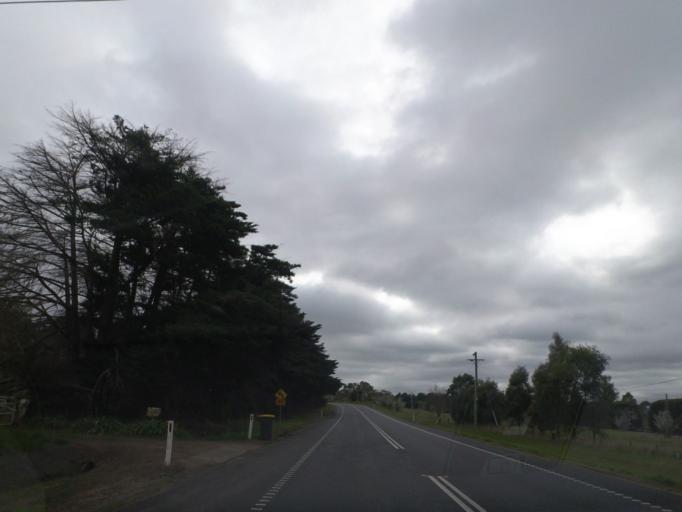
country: AU
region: Victoria
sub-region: Whittlesea
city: Mernda
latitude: -37.5663
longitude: 145.1082
